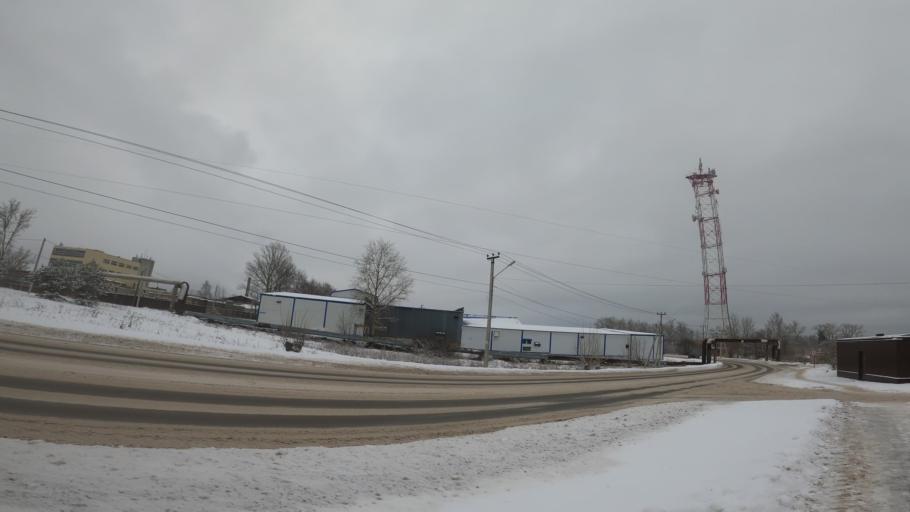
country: RU
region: Jaroslavl
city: Pereslavl'-Zalesskiy
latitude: 56.7482
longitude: 38.8876
